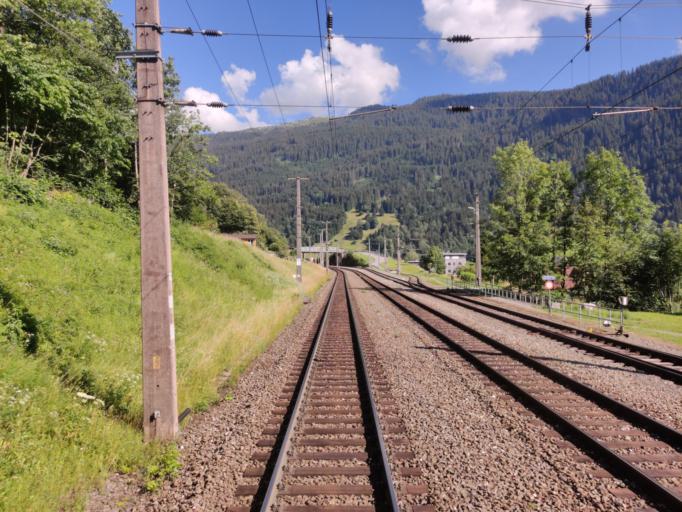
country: AT
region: Vorarlberg
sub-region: Politischer Bezirk Bludenz
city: Dalaas
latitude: 47.1271
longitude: 9.9924
